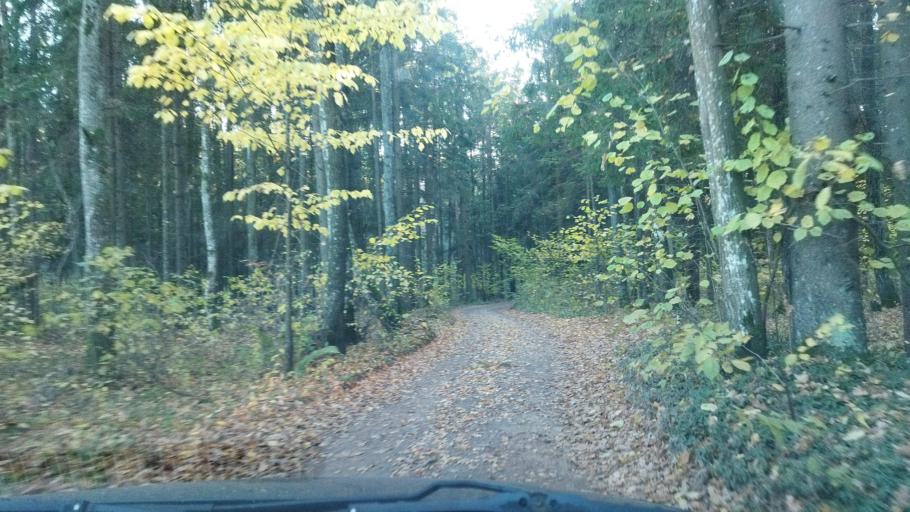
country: BY
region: Minsk
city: Slabada
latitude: 53.9860
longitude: 27.8897
